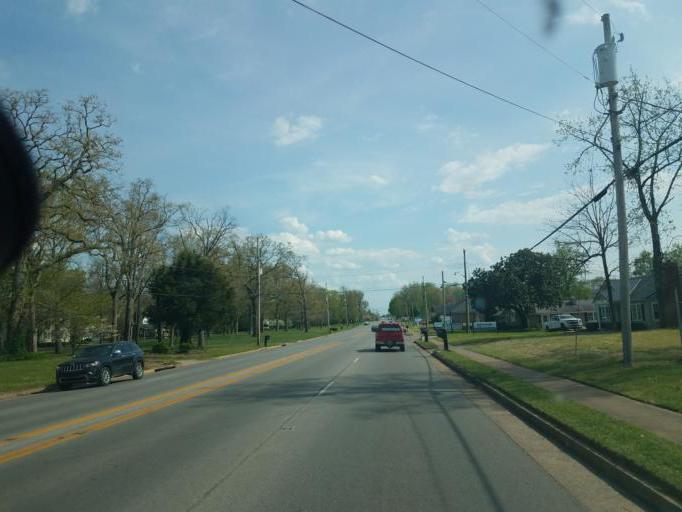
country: US
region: Kentucky
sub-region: Warren County
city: Bowling Green
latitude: 36.9767
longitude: -86.4374
